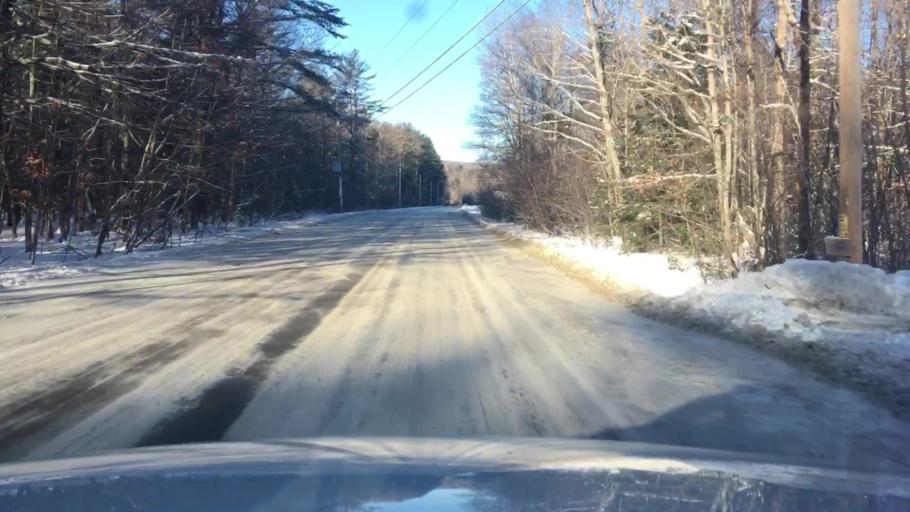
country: US
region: Maine
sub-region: Kennebec County
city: Belgrade
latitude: 44.4277
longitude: -69.8956
